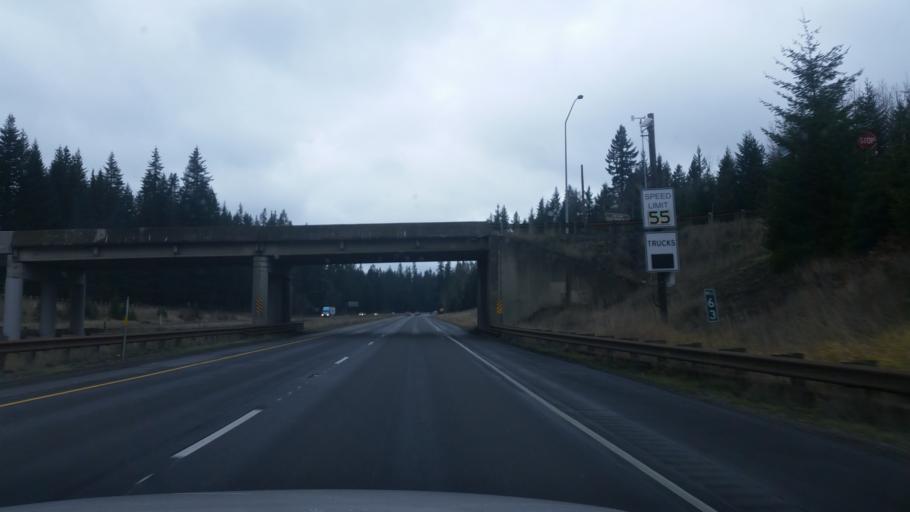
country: US
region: Washington
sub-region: Kittitas County
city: Cle Elum
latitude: 47.3050
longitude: -121.3049
